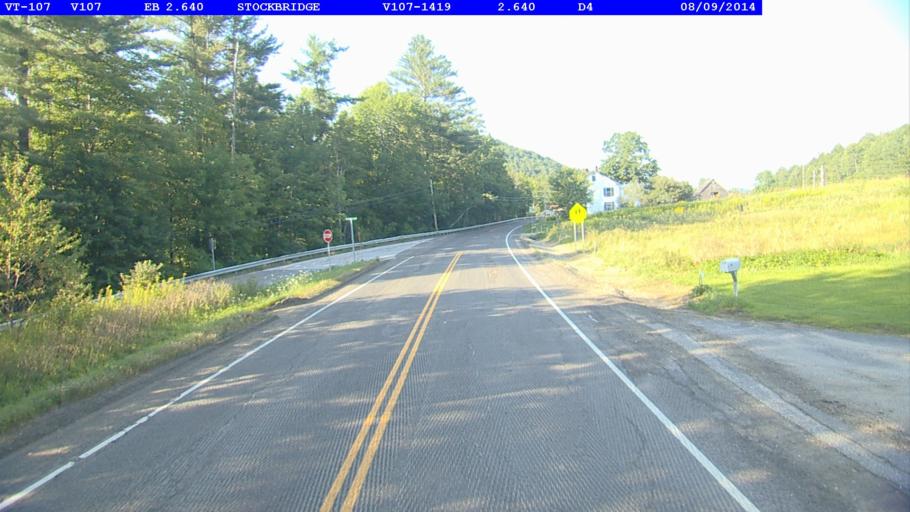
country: US
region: Vermont
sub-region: Orange County
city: Randolph
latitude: 43.7607
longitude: -72.7217
